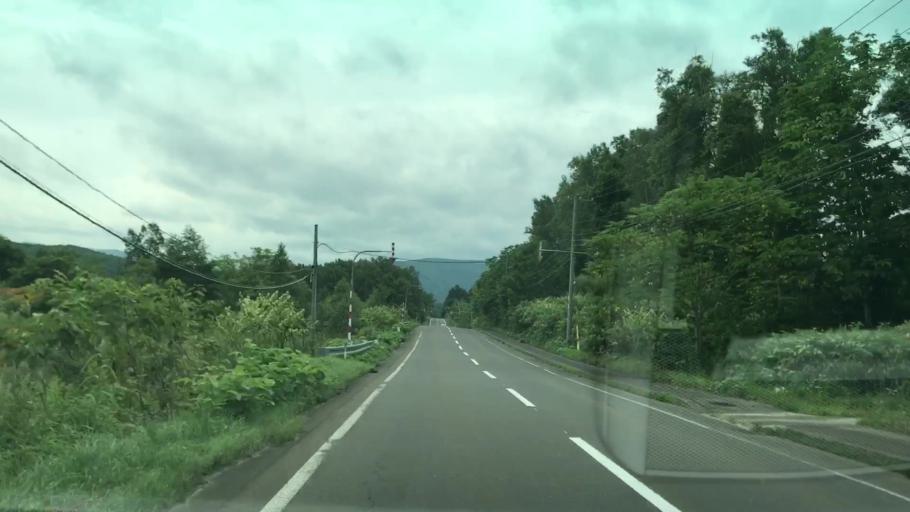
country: JP
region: Hokkaido
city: Yoichi
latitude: 43.0714
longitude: 140.8172
